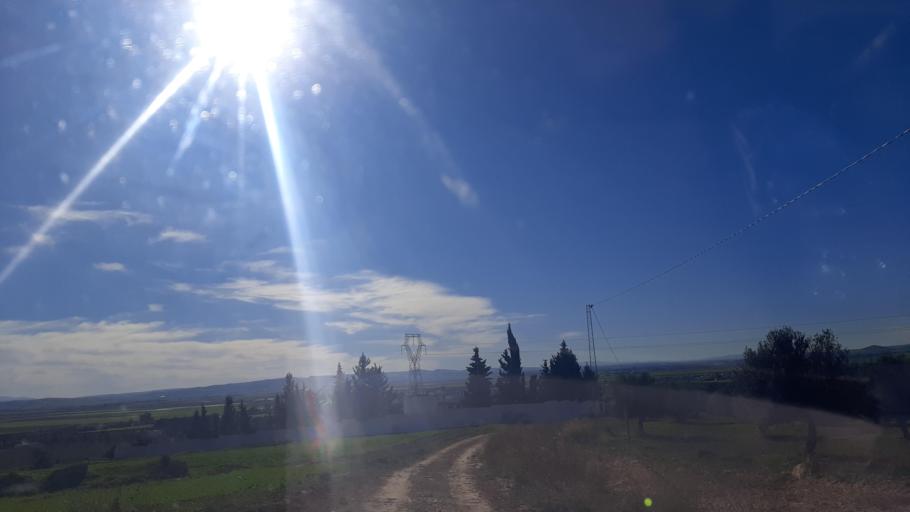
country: TN
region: Tunis
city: Oued Lill
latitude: 36.7640
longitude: 9.9854
